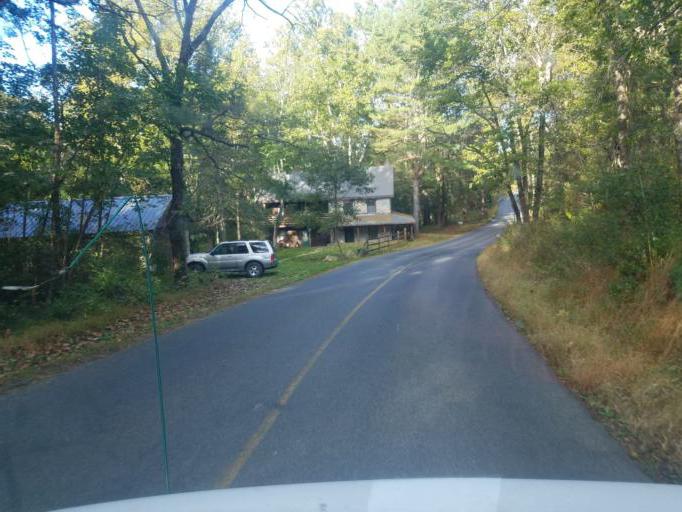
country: US
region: Pennsylvania
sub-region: Adams County
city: Biglerville
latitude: 39.8834
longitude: -77.3292
